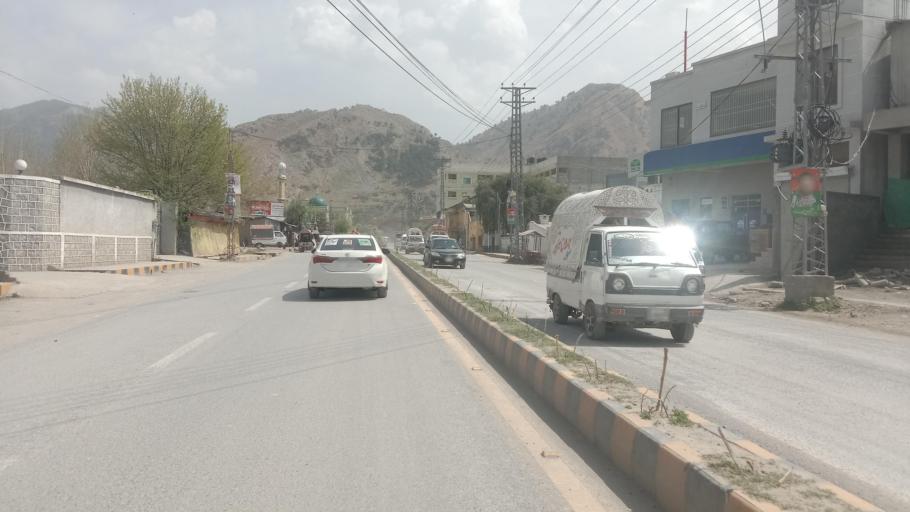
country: PK
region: Khyber Pakhtunkhwa
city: Abbottabad
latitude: 34.1579
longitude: 73.2610
